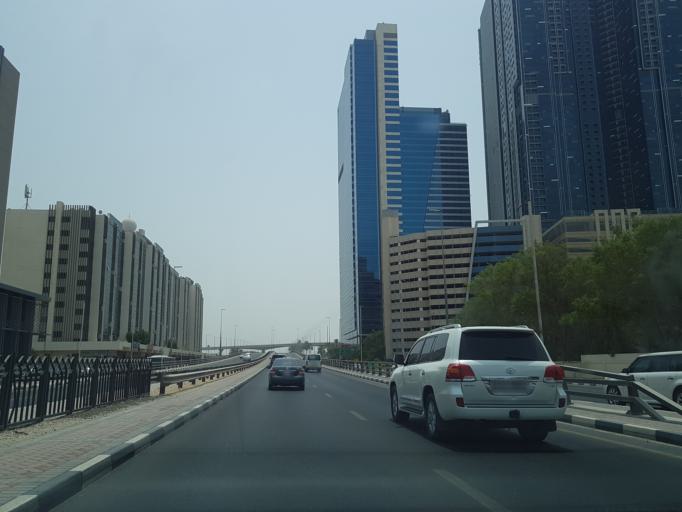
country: AE
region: Ash Shariqah
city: Sharjah
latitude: 25.2317
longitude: 55.2847
